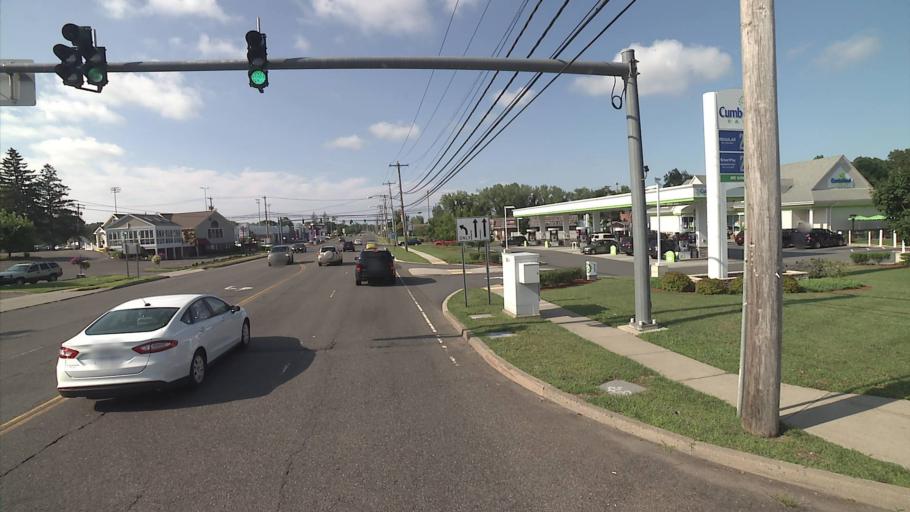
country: US
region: Connecticut
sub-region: New Haven County
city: City of Milford (balance)
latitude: 41.2227
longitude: -73.0729
